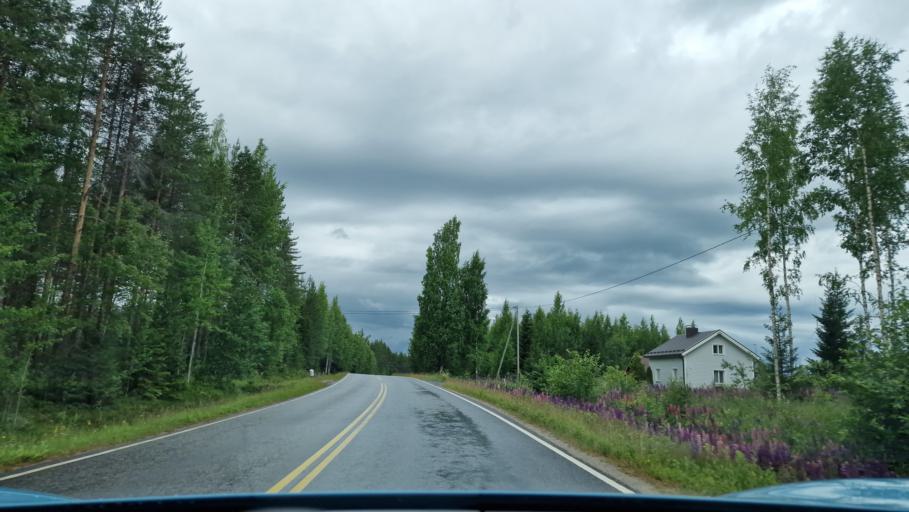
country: FI
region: Southern Ostrobothnia
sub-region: Jaerviseutu
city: Soini
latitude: 62.7182
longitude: 24.4349
